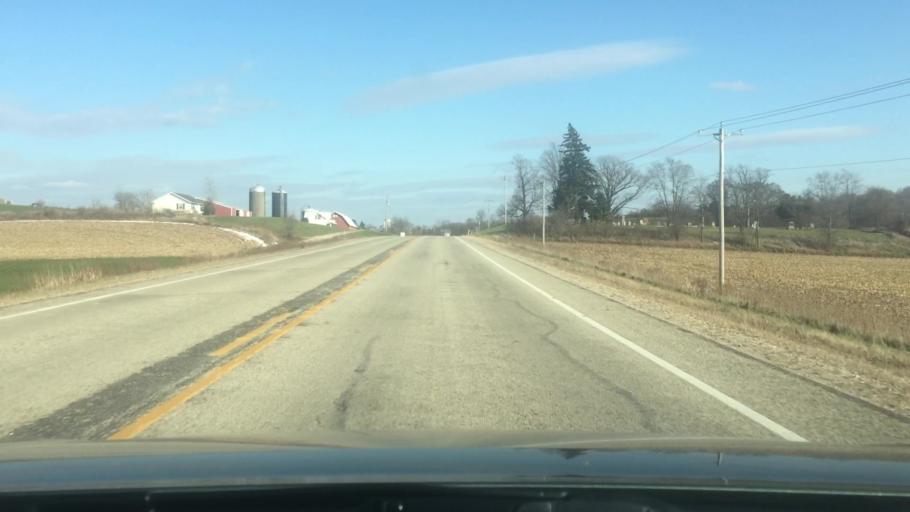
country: US
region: Wisconsin
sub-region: Jefferson County
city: Palmyra
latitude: 42.9326
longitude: -88.6578
